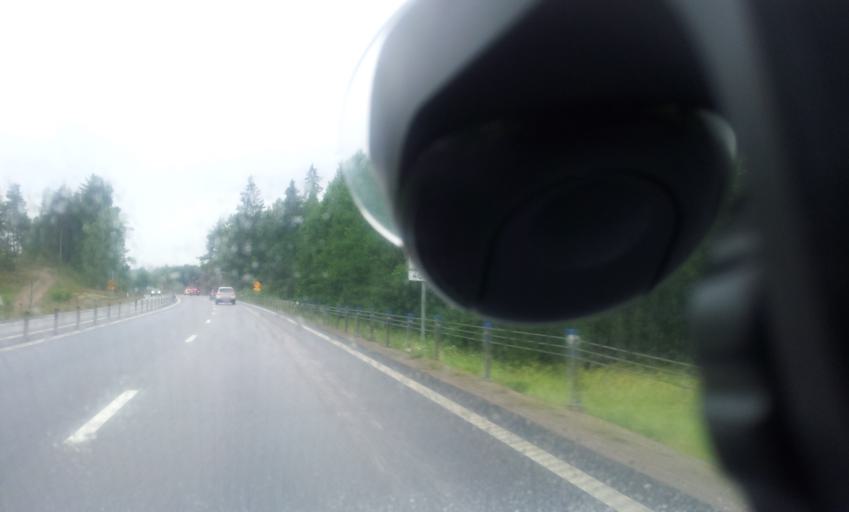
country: SE
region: Kalmar
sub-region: Vasterviks Kommun
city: Forserum
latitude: 57.9862
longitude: 16.4831
